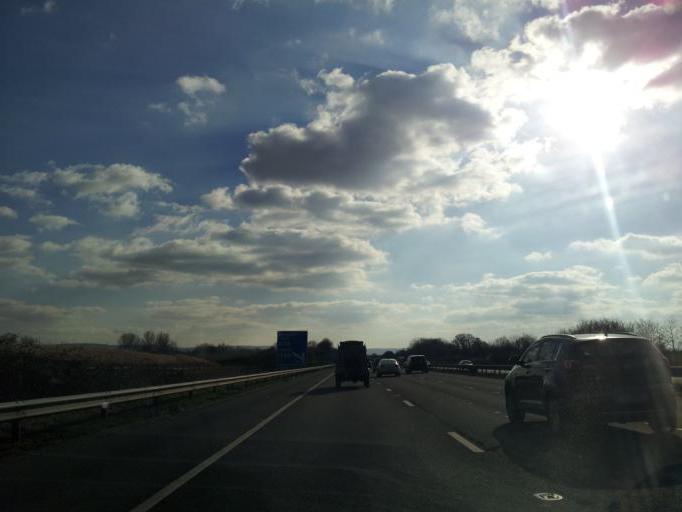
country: GB
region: England
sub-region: Somerset
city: Creech Saint Michael
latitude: 51.0343
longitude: -3.0432
